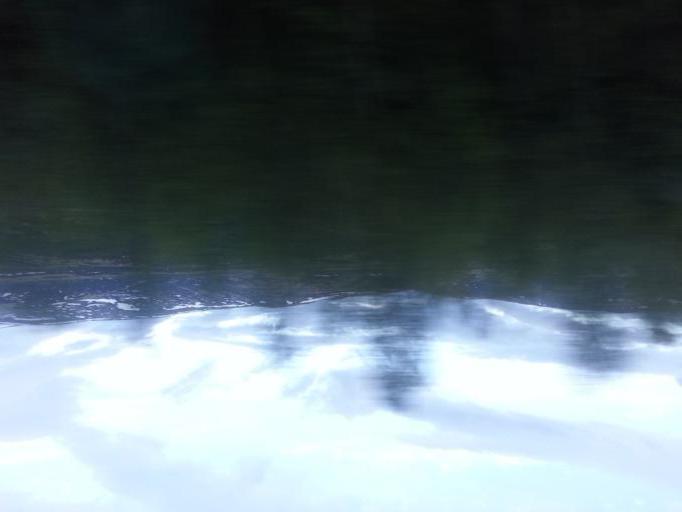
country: NO
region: Oppland
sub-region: Dovre
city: Dovre
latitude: 62.2000
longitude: 9.5205
